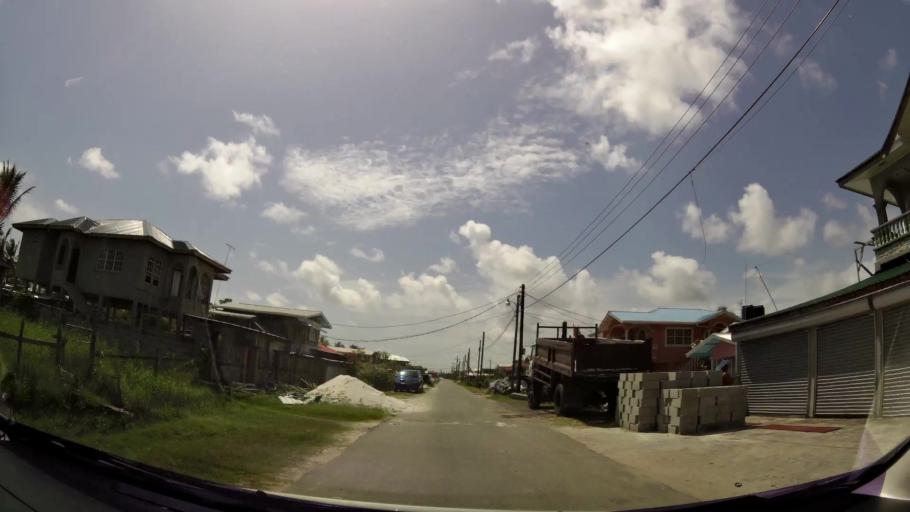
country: GY
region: Demerara-Mahaica
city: Mahaica Village
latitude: 6.7720
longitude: -58.0137
